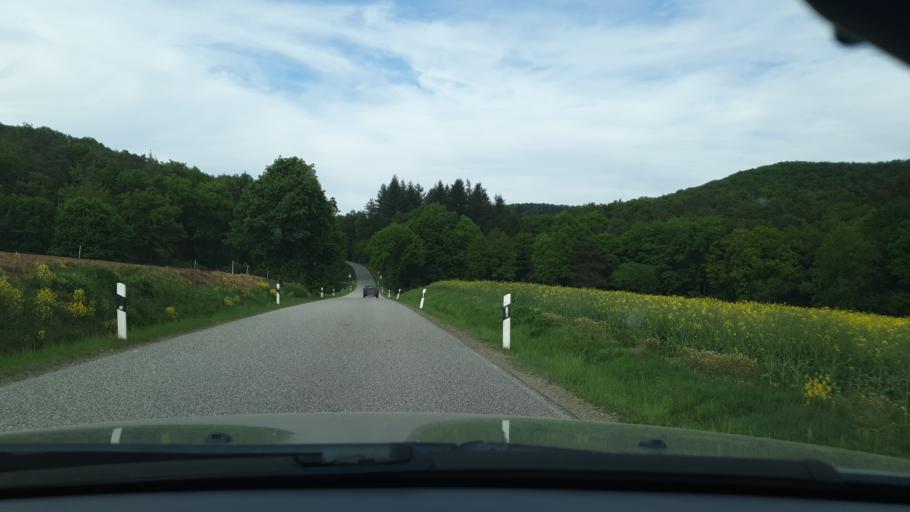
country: DE
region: Rheinland-Pfalz
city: Mittelbrunn
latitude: 49.3819
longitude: 7.5595
